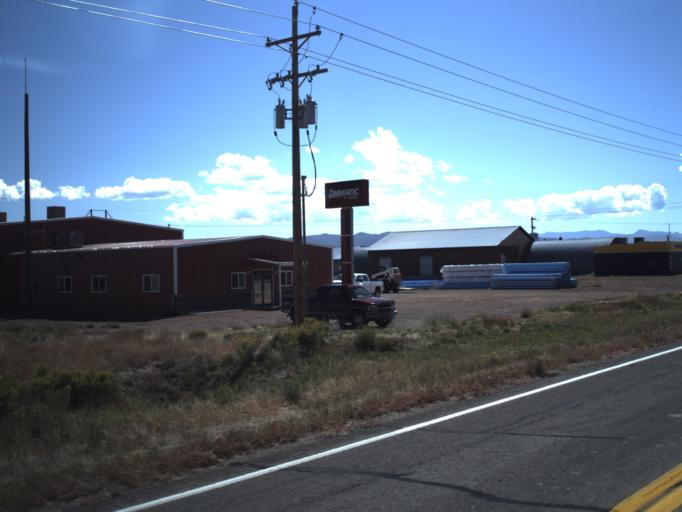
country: US
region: Utah
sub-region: Washington County
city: Enterprise
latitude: 37.7087
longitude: -113.6563
